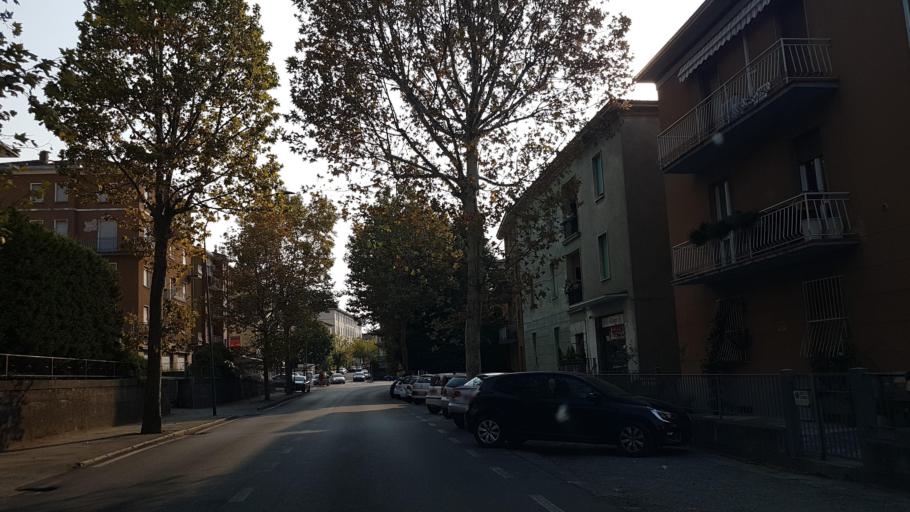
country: IT
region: Emilia-Romagna
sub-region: Provincia di Parma
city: Fornovo di Taro
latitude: 44.6914
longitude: 10.1022
